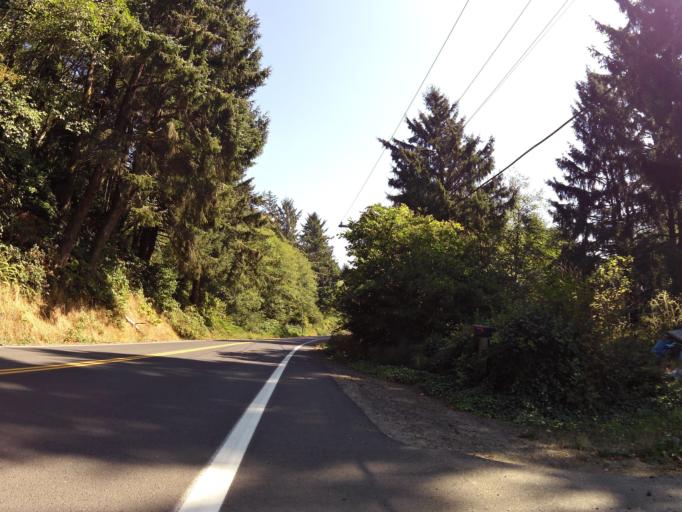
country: US
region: Oregon
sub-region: Tillamook County
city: Pacific City
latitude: 45.1909
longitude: -123.9526
